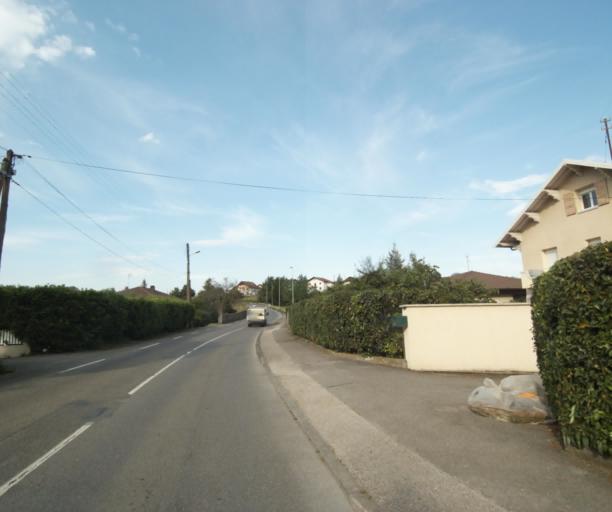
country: FR
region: Rhone-Alpes
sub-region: Departement de la Haute-Savoie
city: Thonon-les-Bains
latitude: 46.3798
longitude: 6.5023
